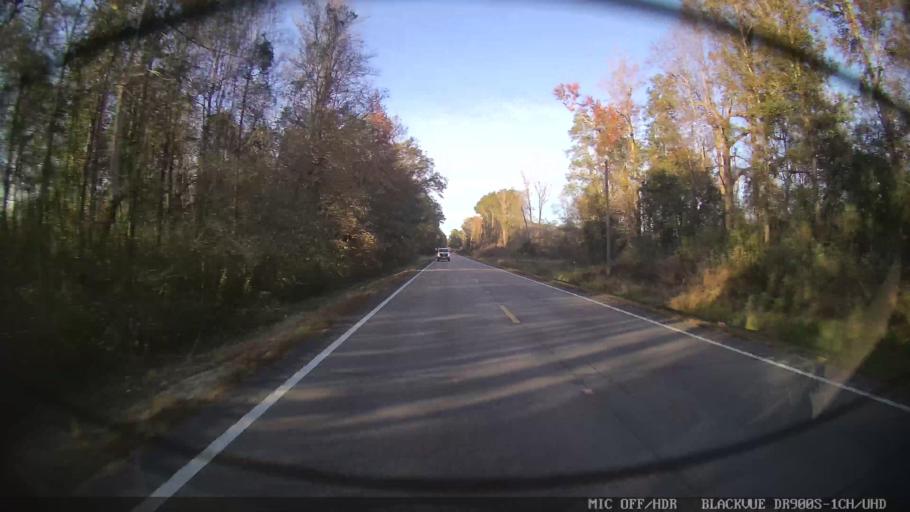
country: US
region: Mississippi
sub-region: Lamar County
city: Lumberton
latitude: 31.0133
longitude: -89.4505
